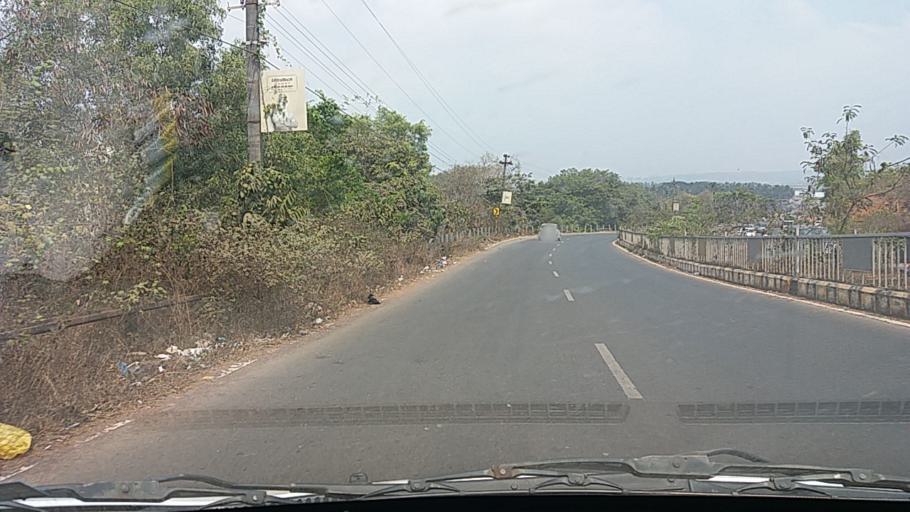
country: IN
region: Goa
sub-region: North Goa
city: Bambolim
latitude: 15.4667
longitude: 73.8514
